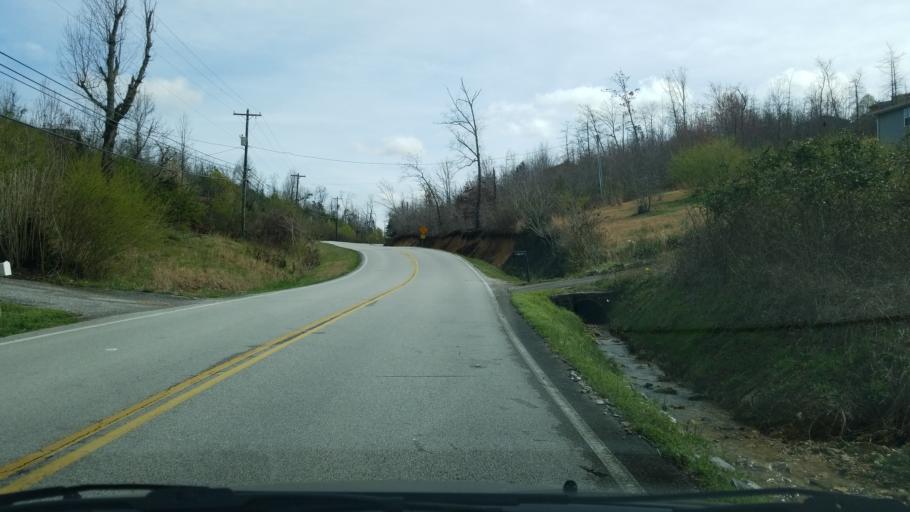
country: US
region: Tennessee
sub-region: Hamilton County
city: Harrison
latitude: 35.1387
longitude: -85.1109
